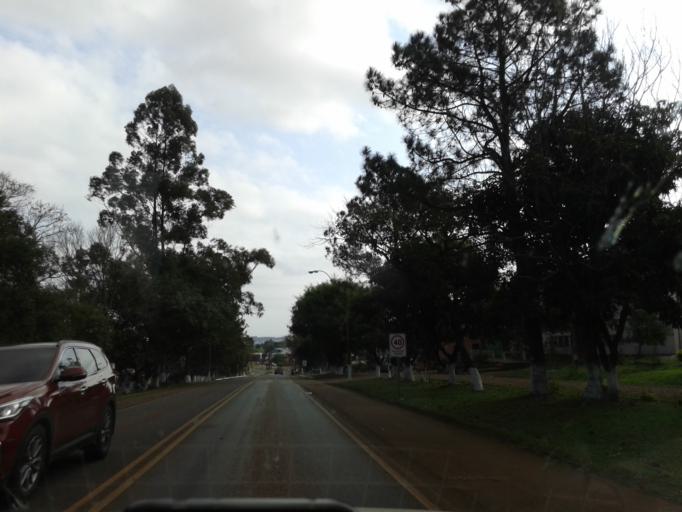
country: PY
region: Itapua
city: Edelira
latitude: -26.7219
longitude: -55.3405
